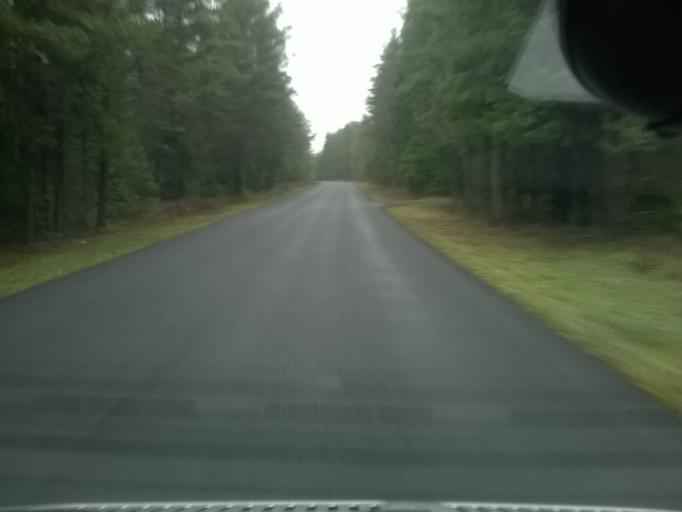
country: EE
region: Harju
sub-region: Nissi vald
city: Riisipere
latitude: 59.1112
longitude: 24.3268
